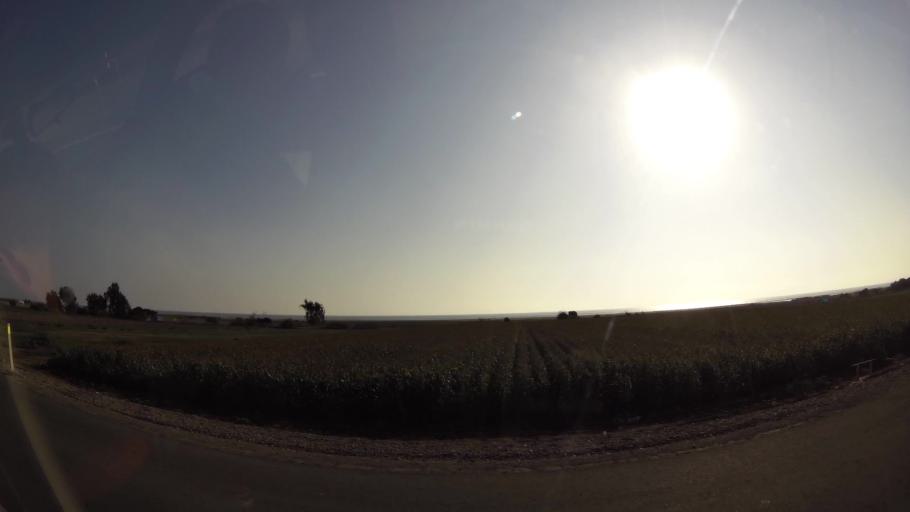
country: PE
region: Ica
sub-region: Provincia de Chincha
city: Chincha Baja
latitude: -13.5323
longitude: -76.1831
